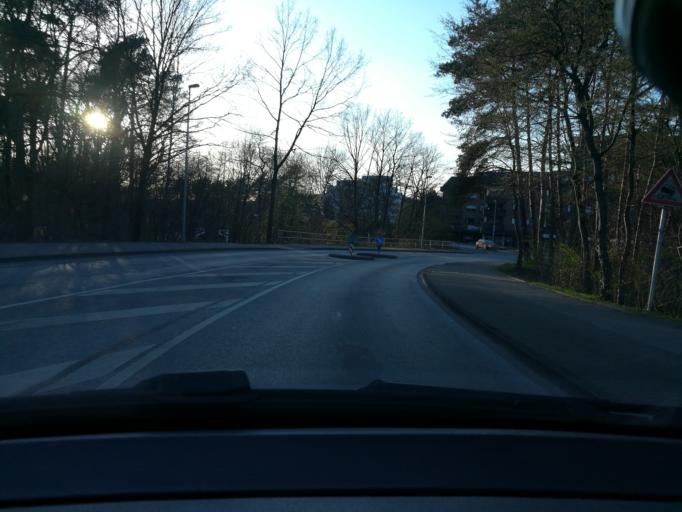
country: DE
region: North Rhine-Westphalia
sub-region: Regierungsbezirk Detmold
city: Oerlinghausen
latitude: 51.9433
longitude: 8.5826
